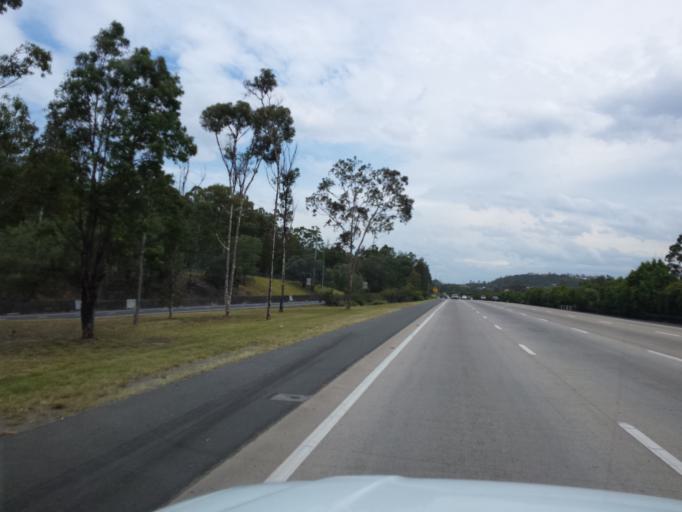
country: AU
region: Queensland
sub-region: Gold Coast
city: Oxenford
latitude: -27.9082
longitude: 153.3178
